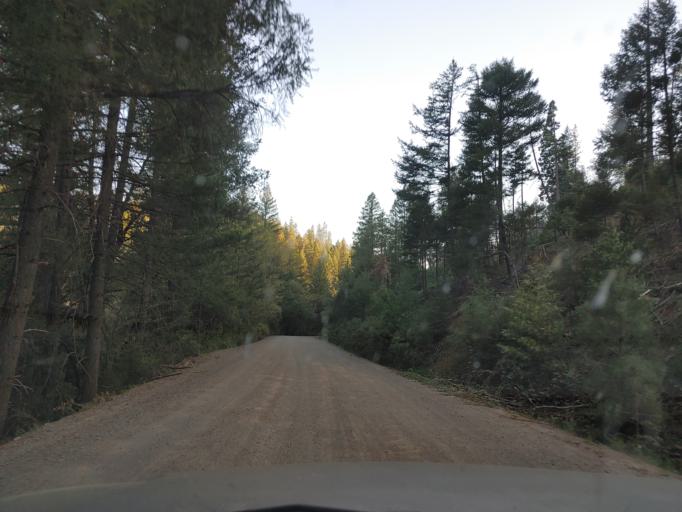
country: US
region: California
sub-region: Shasta County
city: Bella Vista
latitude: 40.8145
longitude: -121.9941
